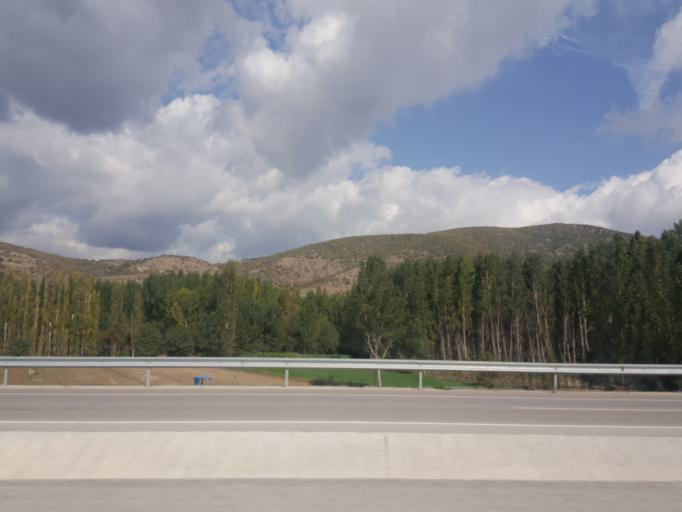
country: TR
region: Tokat
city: Gokdere
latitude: 40.3803
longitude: 36.6846
